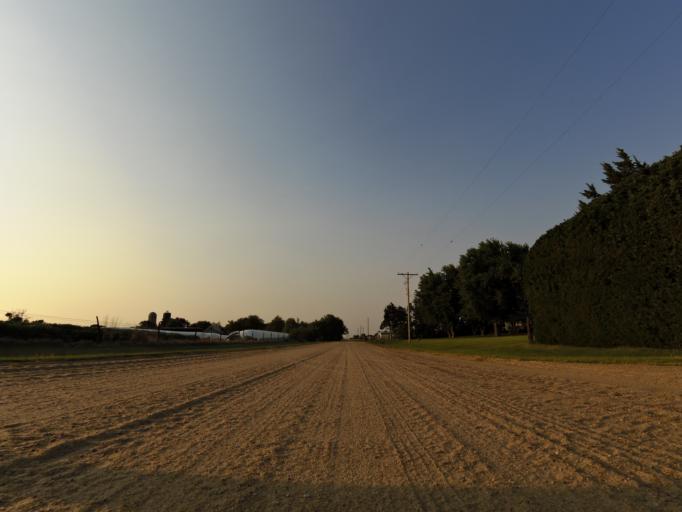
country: US
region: Kansas
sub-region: Reno County
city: South Hutchinson
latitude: 38.0107
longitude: -97.9954
